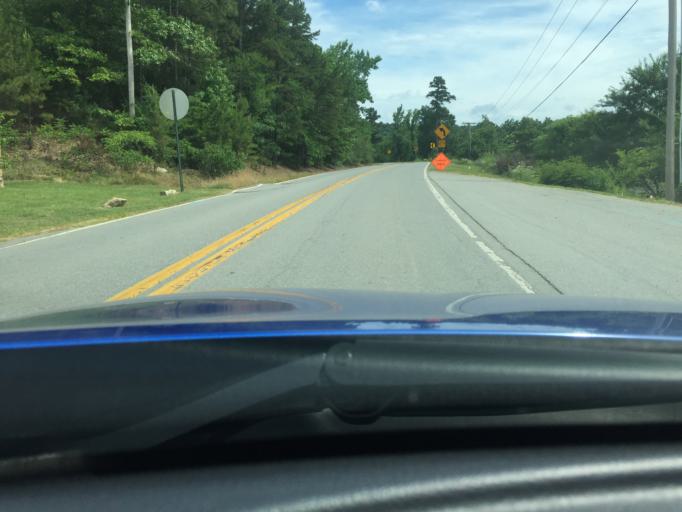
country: US
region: Arkansas
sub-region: Pulaski County
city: Maumelle
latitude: 34.8124
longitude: -92.4431
